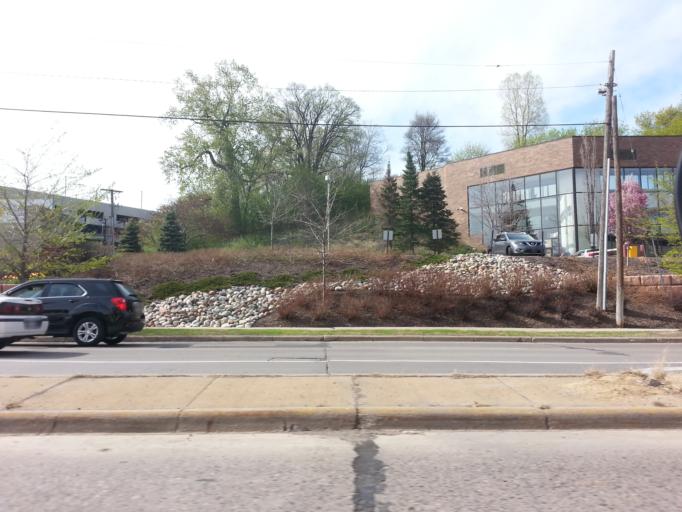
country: US
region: Minnesota
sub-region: Ramsey County
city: Saint Paul
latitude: 44.9561
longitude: -93.0966
